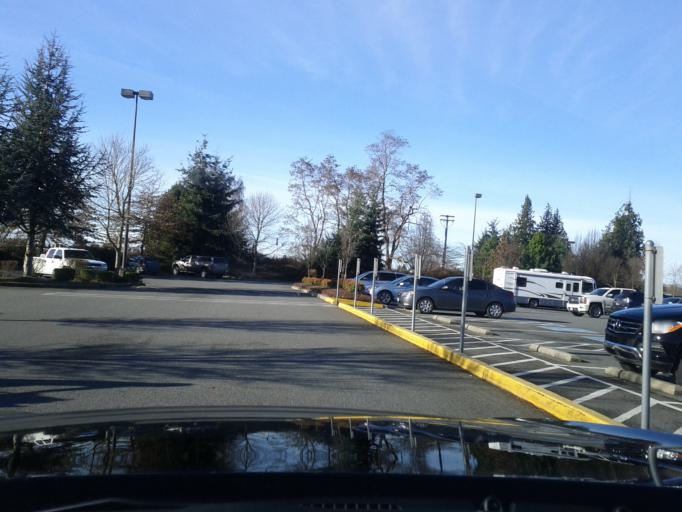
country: US
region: Washington
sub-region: Skagit County
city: Burlington
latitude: 48.4536
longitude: -122.3387
